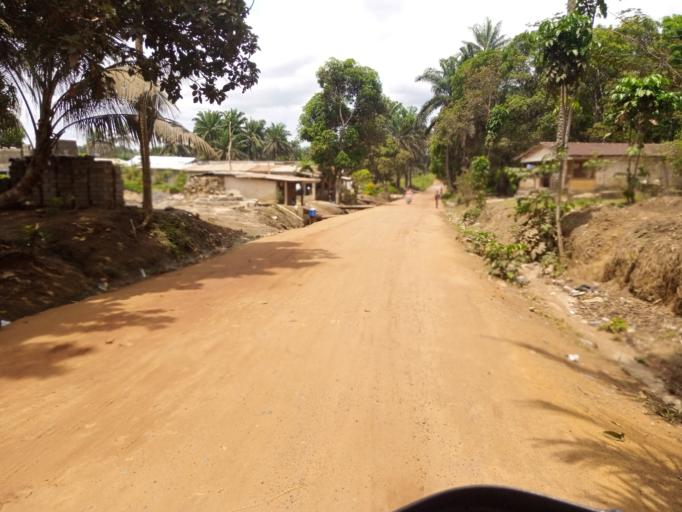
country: SL
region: Western Area
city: Waterloo
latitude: 8.3343
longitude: -13.0046
